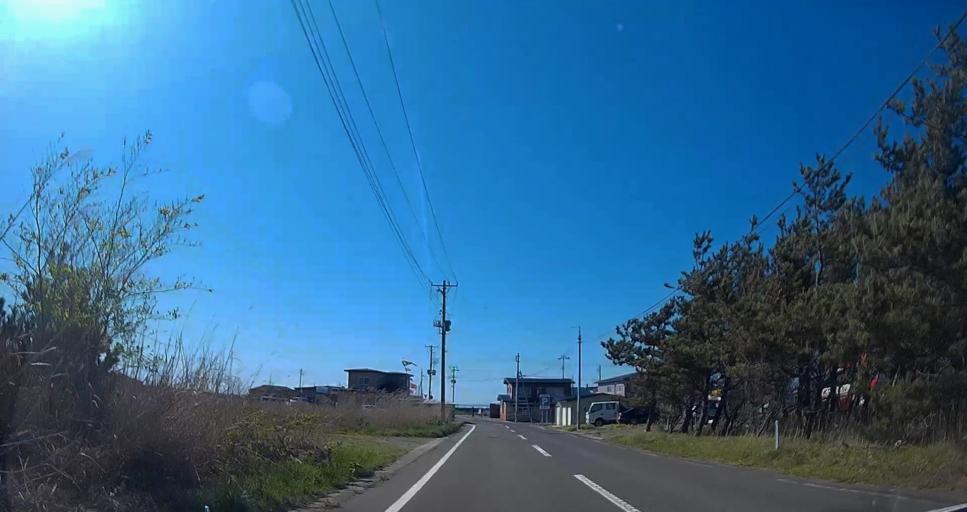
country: JP
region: Hokkaido
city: Hakodate
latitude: 41.5449
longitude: 140.9134
